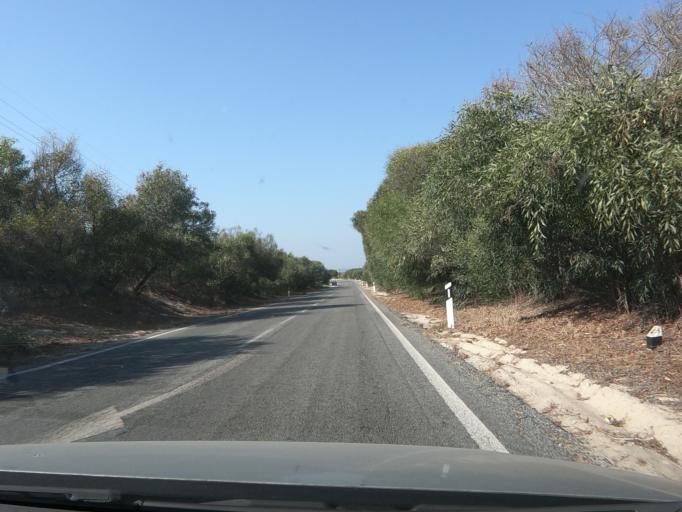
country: PT
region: Setubal
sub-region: Setubal
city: Setubal
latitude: 38.4144
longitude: -8.8152
